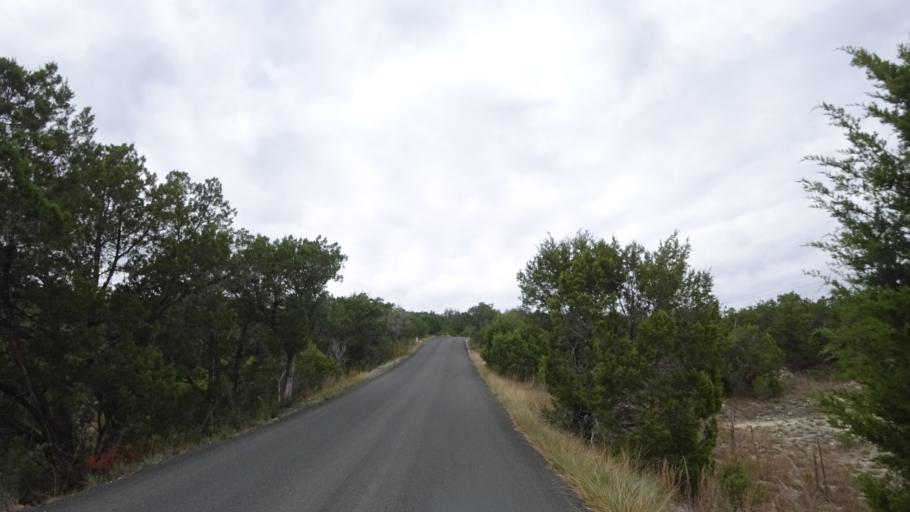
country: US
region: Texas
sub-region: Travis County
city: Bee Cave
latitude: 30.3457
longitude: -97.9349
